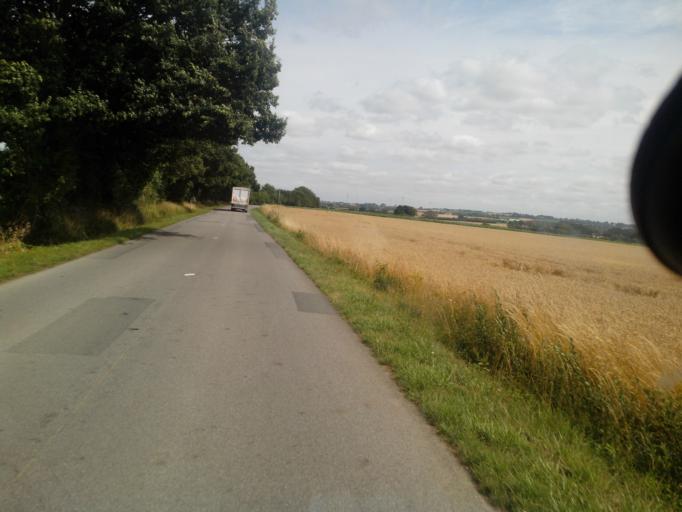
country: FR
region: Brittany
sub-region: Departement d'Ille-et-Vilaine
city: Messac
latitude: 47.8123
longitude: -1.8054
